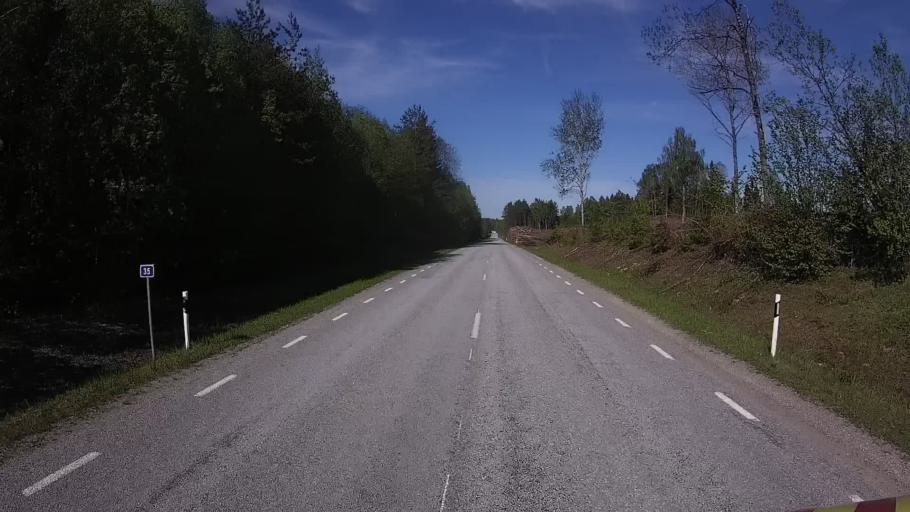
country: EE
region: Vorumaa
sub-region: Antsla vald
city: Vana-Antsla
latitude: 57.9863
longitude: 26.4790
